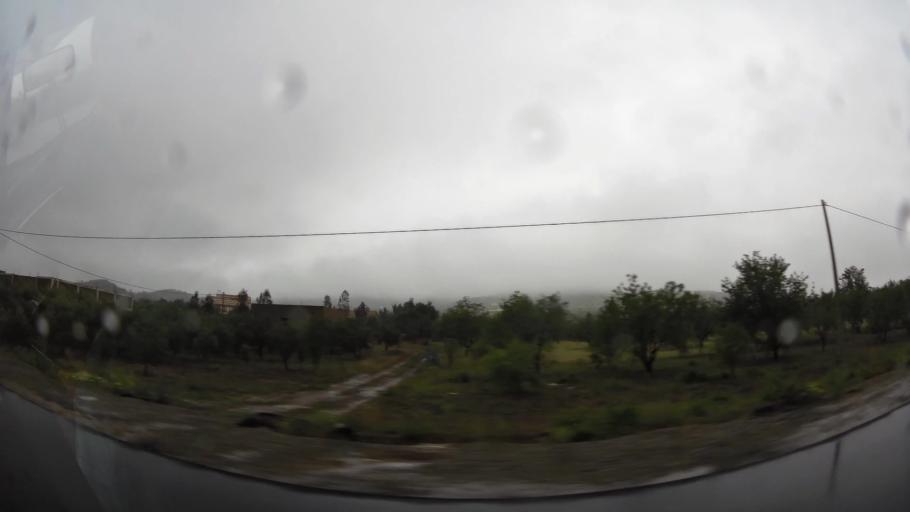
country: MA
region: Oriental
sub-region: Nador
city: Midar
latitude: 34.8539
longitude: -3.7220
